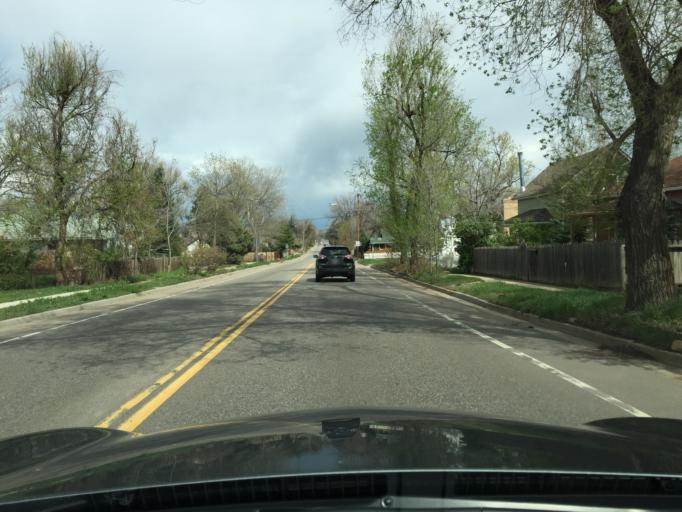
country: US
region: Colorado
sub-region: Boulder County
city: Lafayette
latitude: 40.0002
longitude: -105.0865
